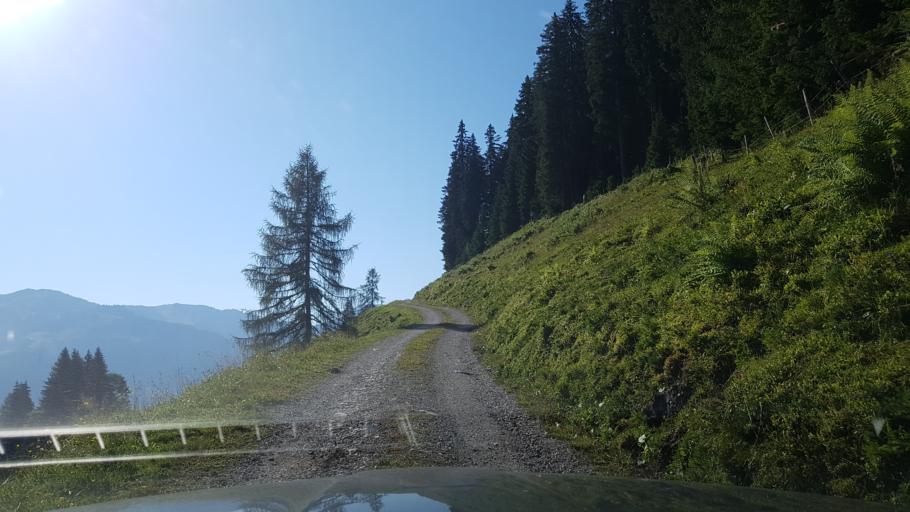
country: AT
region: Salzburg
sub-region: Politischer Bezirk Sankt Johann im Pongau
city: Dorfgastein
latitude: 47.2480
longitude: 13.0704
